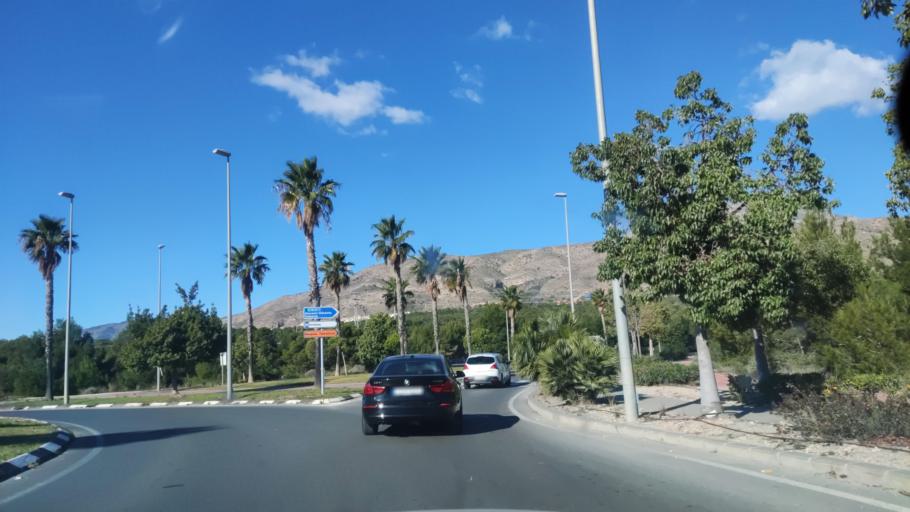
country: ES
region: Valencia
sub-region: Provincia de Alicante
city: Benidorm
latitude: 38.5456
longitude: -0.1610
